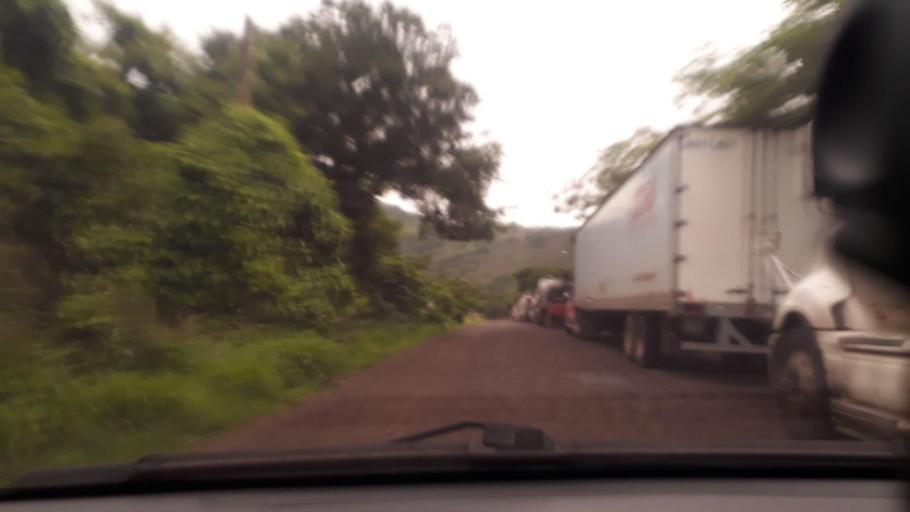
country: GT
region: Jutiapa
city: Atescatempa
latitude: 14.2286
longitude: -89.7056
